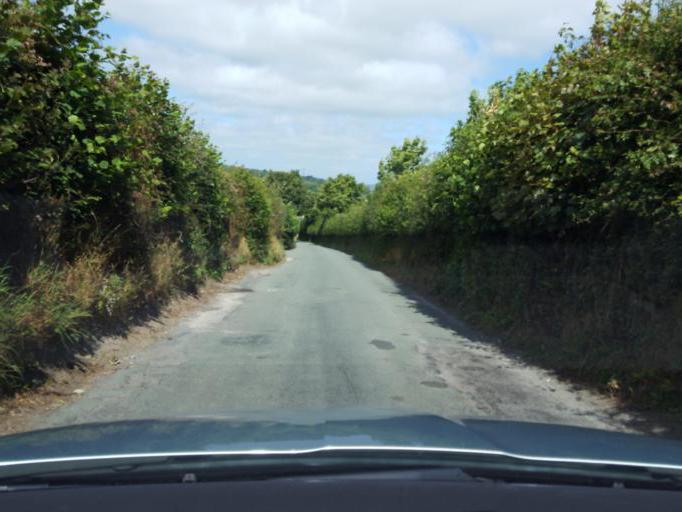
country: GB
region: Wales
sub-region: County of Flintshire
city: Leeswood
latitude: 53.1204
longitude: -3.1336
